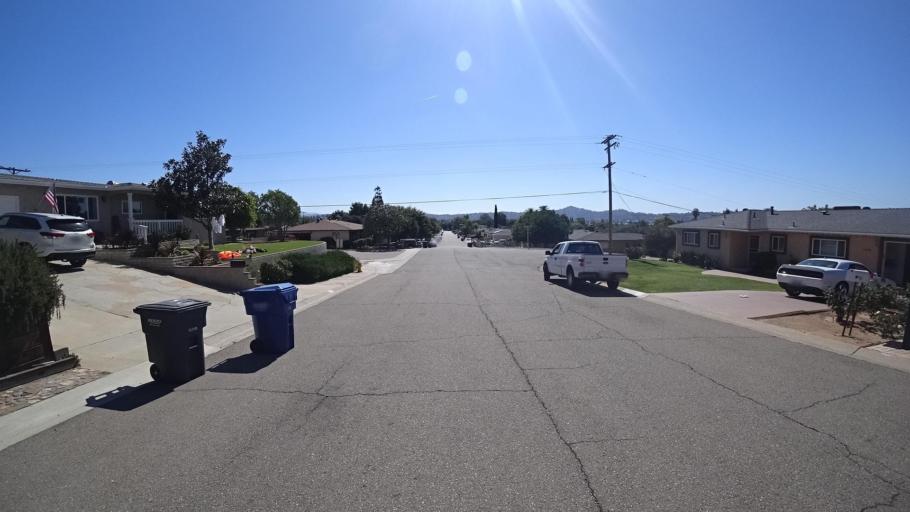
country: US
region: California
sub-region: San Diego County
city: Santee
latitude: 32.8285
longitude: -116.9576
